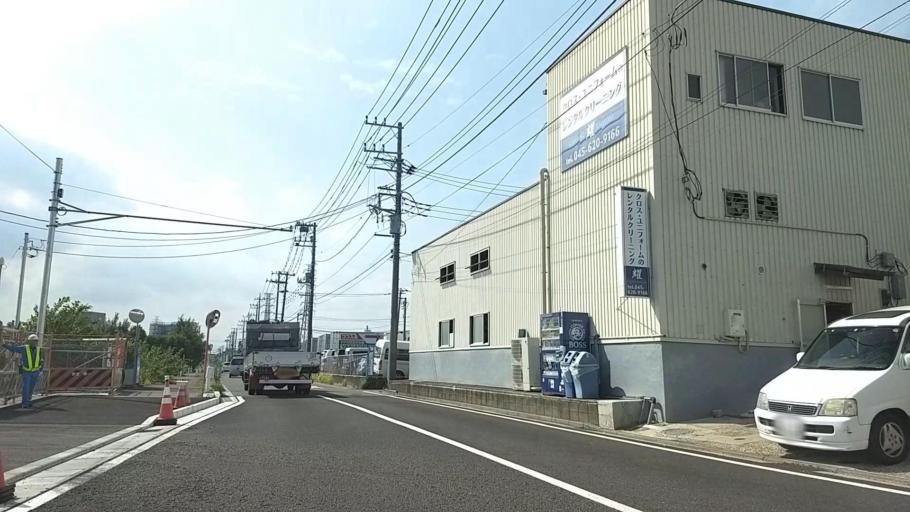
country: JP
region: Kanagawa
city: Yokohama
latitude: 35.5168
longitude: 139.5895
